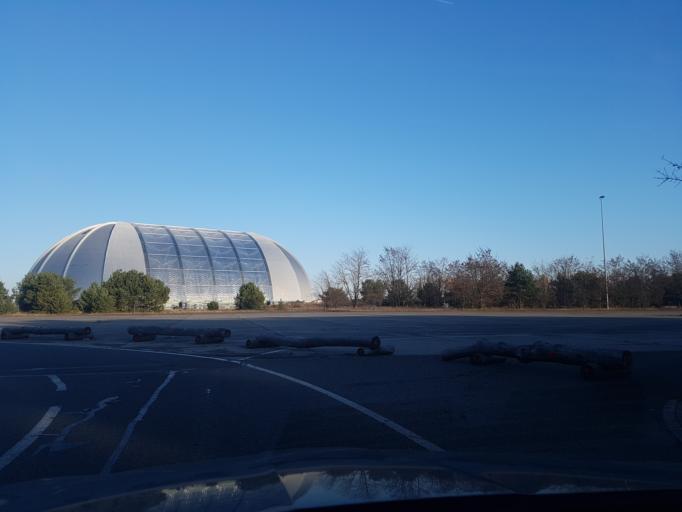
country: DE
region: Brandenburg
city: Halbe
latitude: 52.0325
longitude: 13.7481
